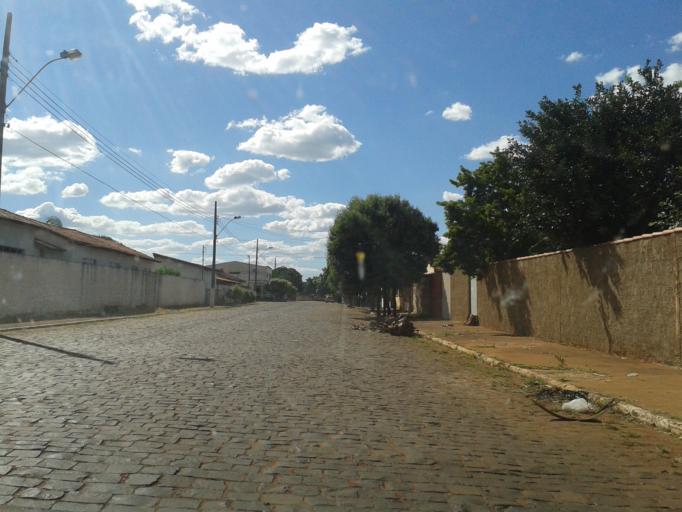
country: BR
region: Minas Gerais
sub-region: Santa Vitoria
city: Santa Vitoria
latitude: -18.6936
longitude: -49.9460
